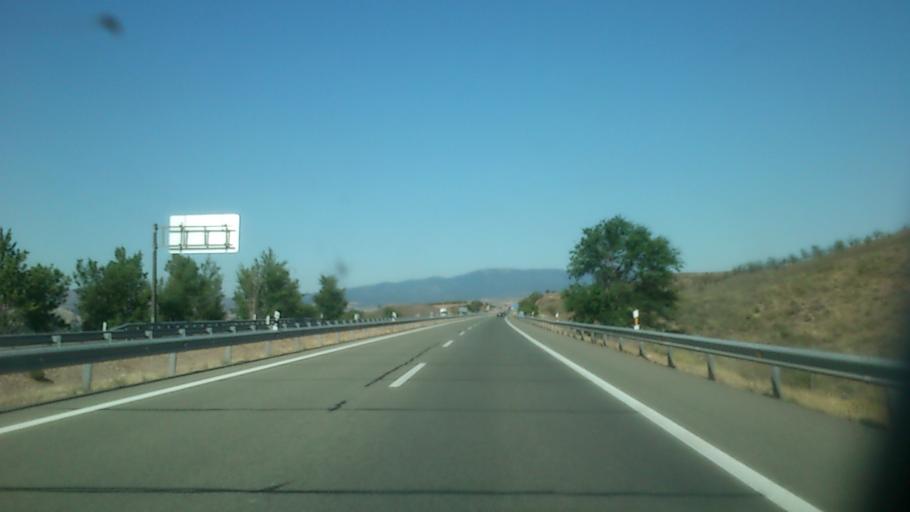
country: ES
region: Aragon
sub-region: Provincia de Zaragoza
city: Terrer
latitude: 41.3178
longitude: -1.6952
